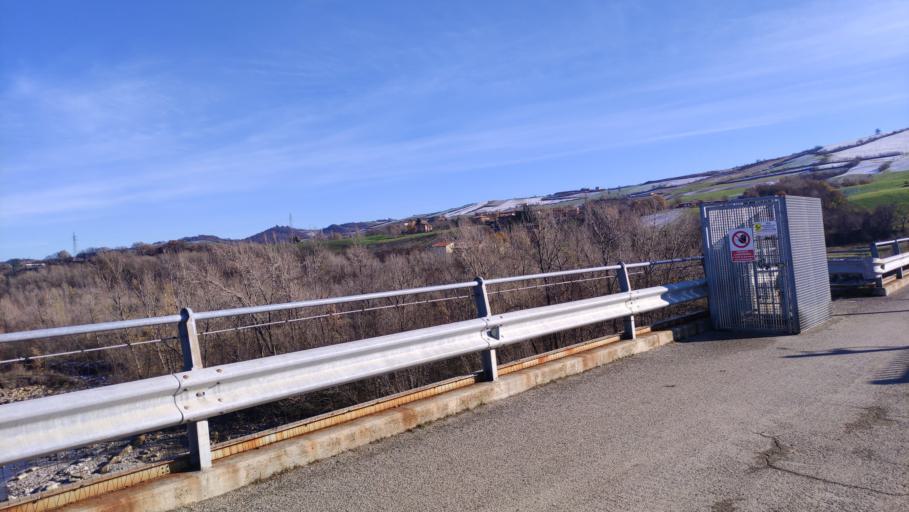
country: IT
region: Emilia-Romagna
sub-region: Provincia di Reggio Emilia
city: Castellarano
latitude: 44.5041
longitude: 10.7297
